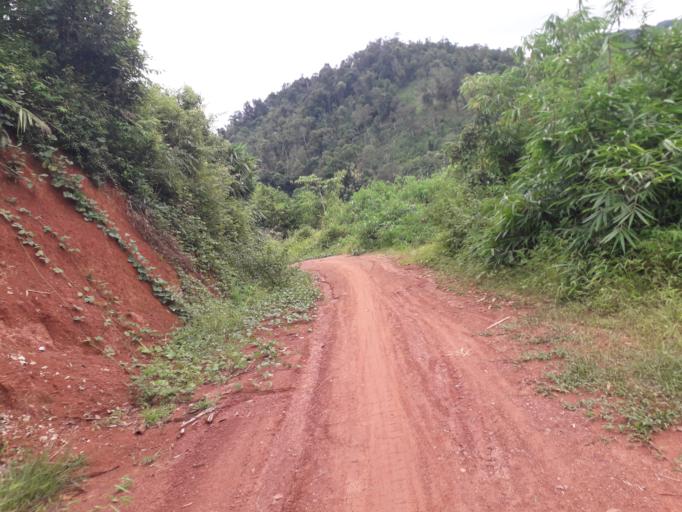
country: CN
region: Yunnan
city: Menglie
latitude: 22.2024
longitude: 101.6725
